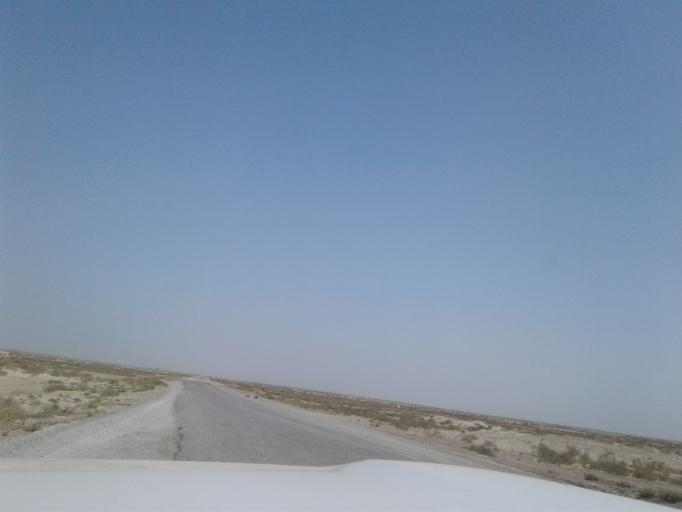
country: IR
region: Golestan
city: Gomishan
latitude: 37.9281
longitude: 53.8456
